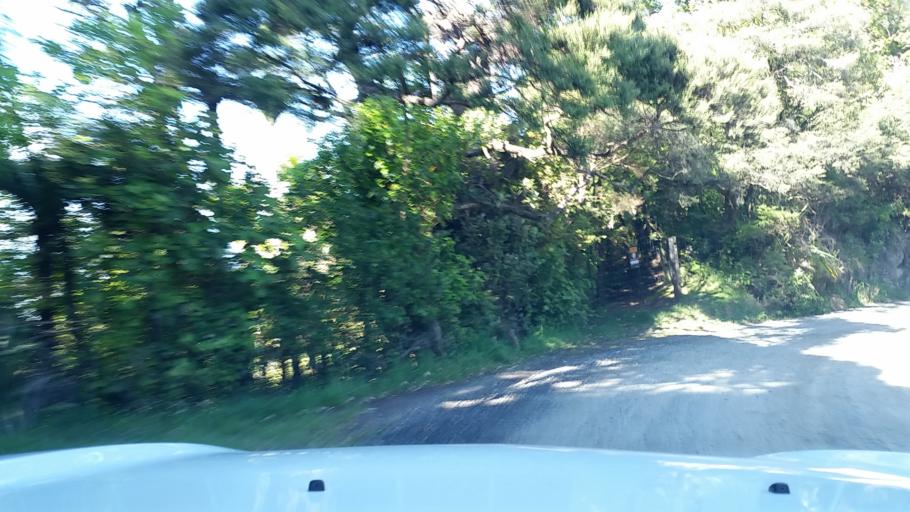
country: NZ
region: Auckland
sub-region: Auckland
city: Titirangi
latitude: -37.0306
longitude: 174.5252
